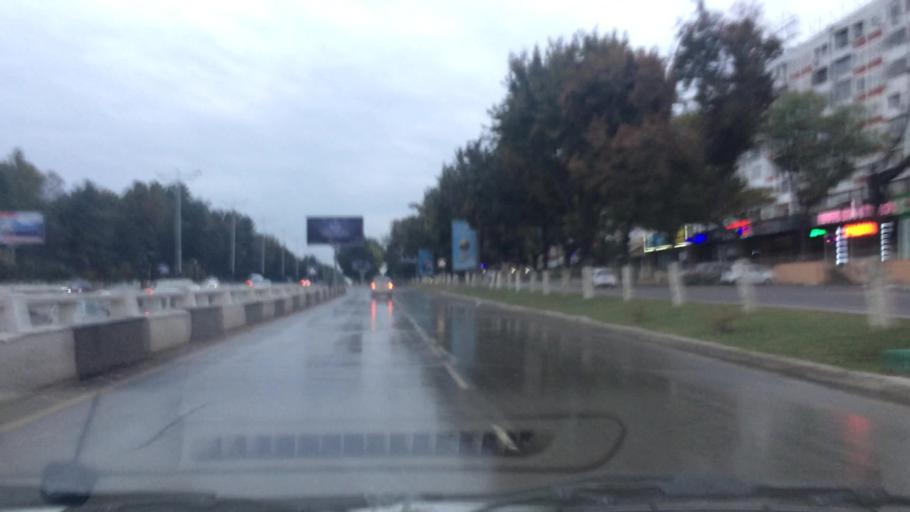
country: UZ
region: Toshkent Shahri
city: Tashkent
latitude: 41.3089
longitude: 69.2387
